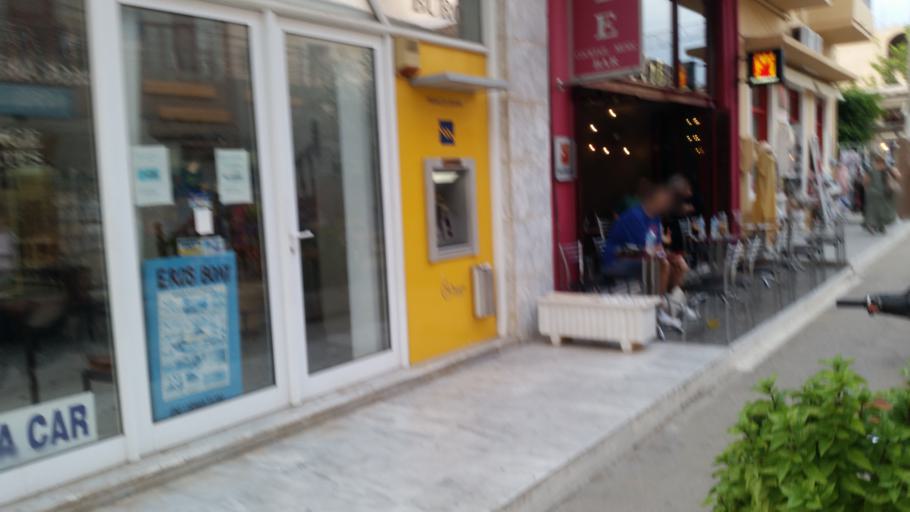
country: GR
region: Peloponnese
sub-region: Nomos Argolidos
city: Tolon
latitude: 37.5205
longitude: 22.8592
